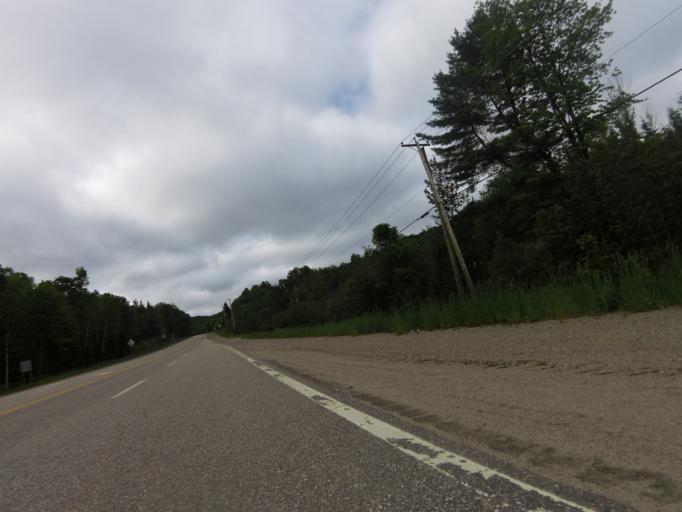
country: CA
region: Quebec
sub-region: Outaouais
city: Shawville
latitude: 45.8356
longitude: -76.4605
